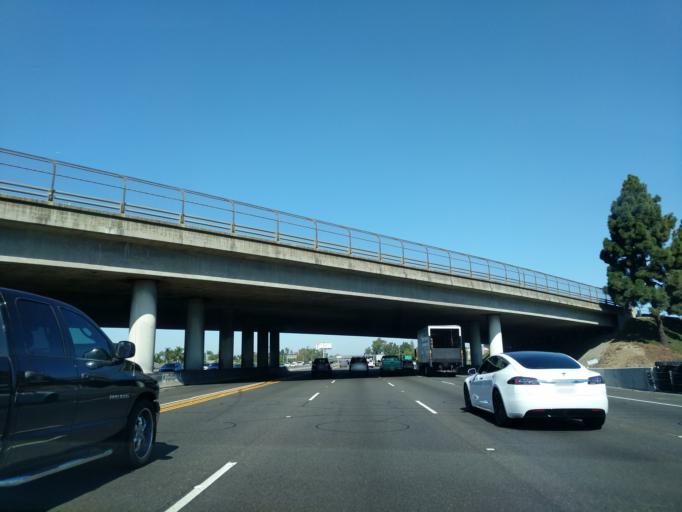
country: US
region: California
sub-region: Orange County
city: Fountain Valley
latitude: 33.7051
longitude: -117.9539
